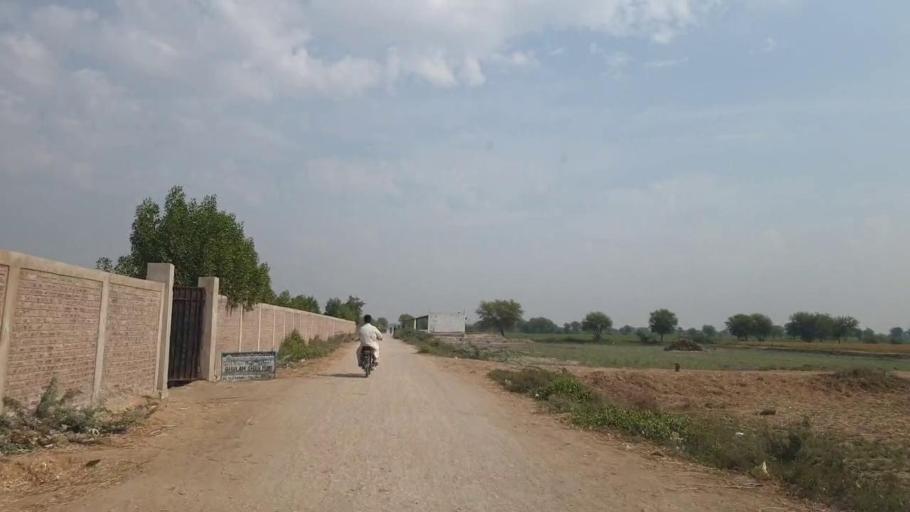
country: PK
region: Sindh
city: Rajo Khanani
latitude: 24.9539
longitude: 68.9788
